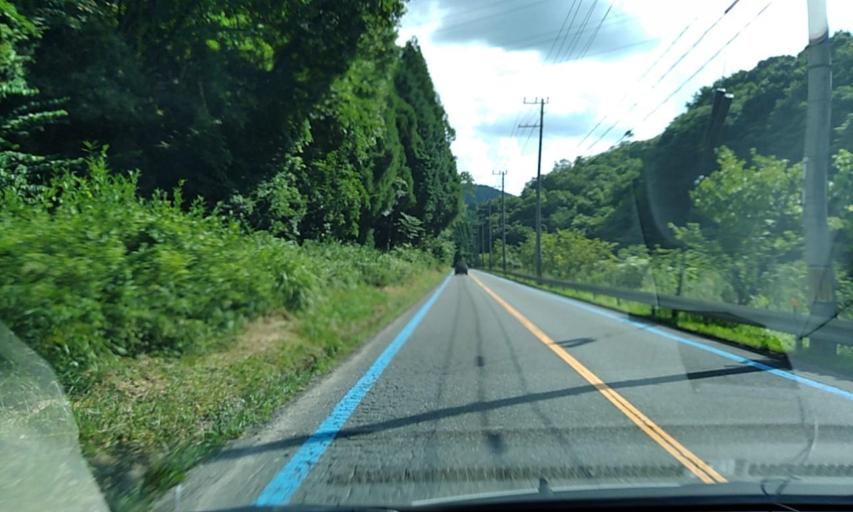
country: JP
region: Kyoto
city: Ayabe
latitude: 35.3086
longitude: 135.2994
